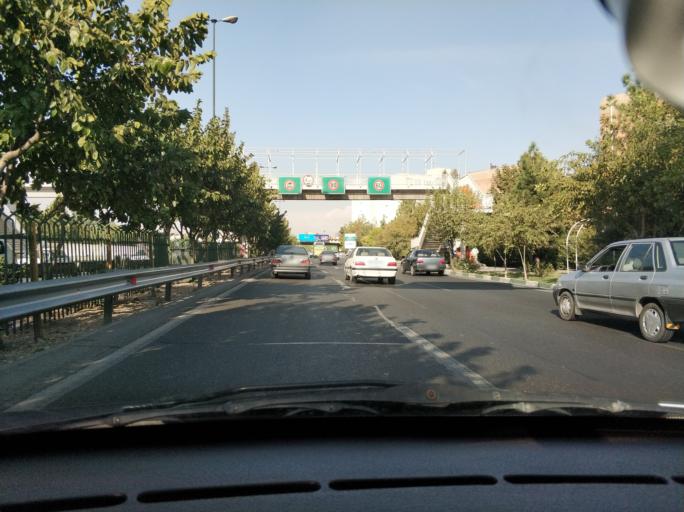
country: IR
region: Tehran
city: Tehran
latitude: 35.7271
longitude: 51.3670
